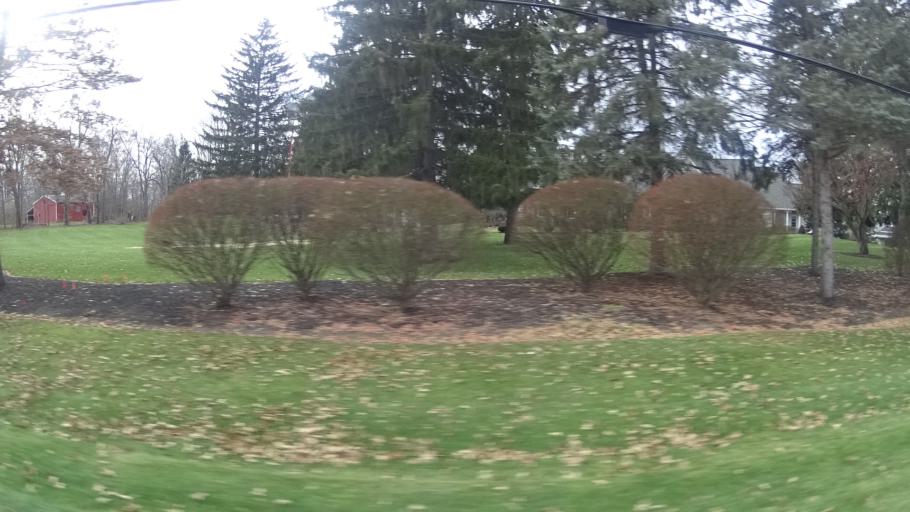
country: US
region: Ohio
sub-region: Cuyahoga County
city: Olmsted Falls
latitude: 41.3092
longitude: -81.9144
